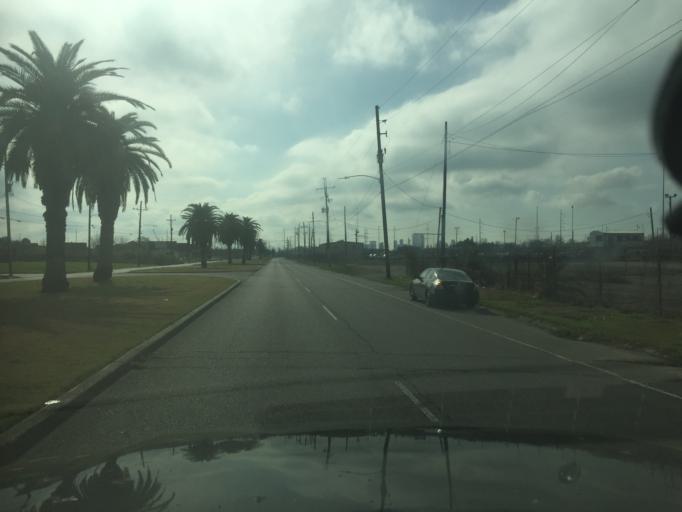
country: US
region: Louisiana
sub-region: Orleans Parish
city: New Orleans
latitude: 29.9960
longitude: -90.0421
